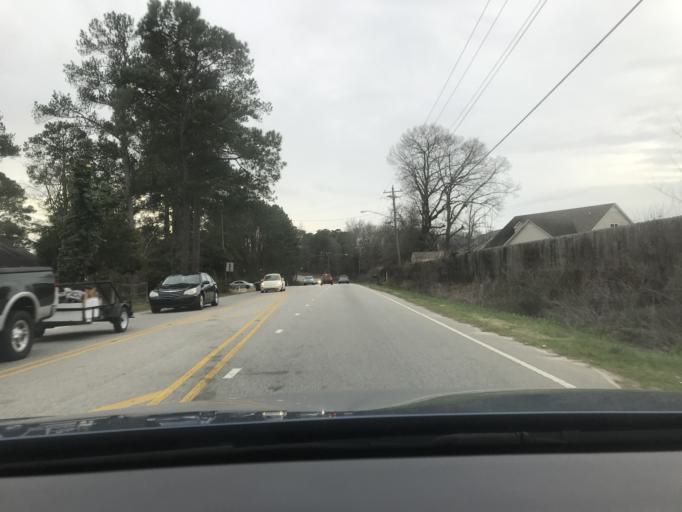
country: US
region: North Carolina
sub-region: Hoke County
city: Rockfish
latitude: 35.0305
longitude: -78.9994
